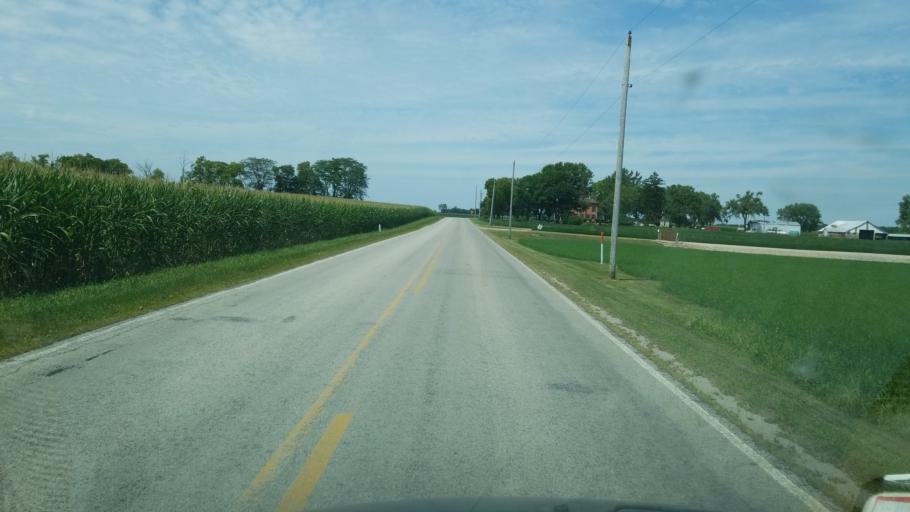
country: US
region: Ohio
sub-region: Madison County
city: West Jefferson
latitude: 39.9560
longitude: -83.2724
